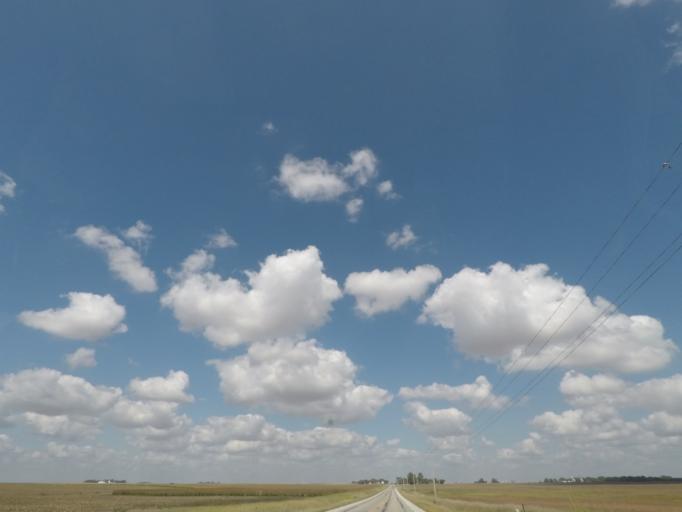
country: US
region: Iowa
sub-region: Story County
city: Nevada
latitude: 42.0541
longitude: -93.4057
